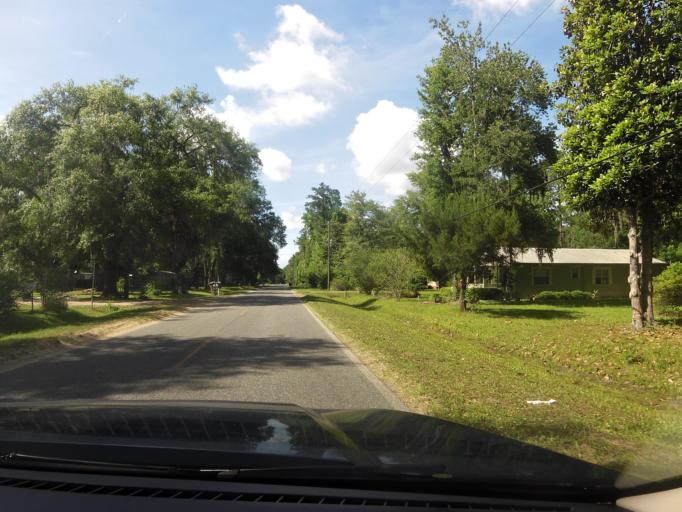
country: US
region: Florida
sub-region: Nassau County
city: Hilliard
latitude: 30.6777
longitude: -81.9216
